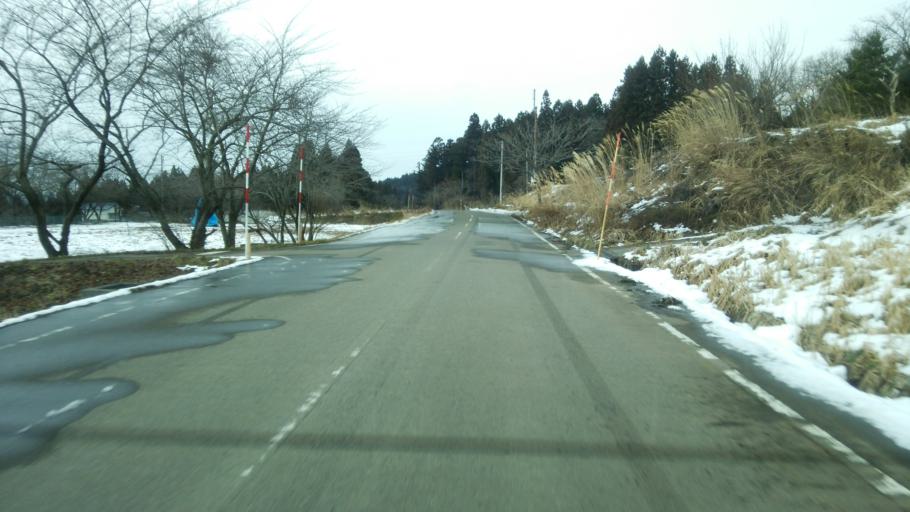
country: JP
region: Fukushima
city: Inawashiro
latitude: 37.5683
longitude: 139.9920
